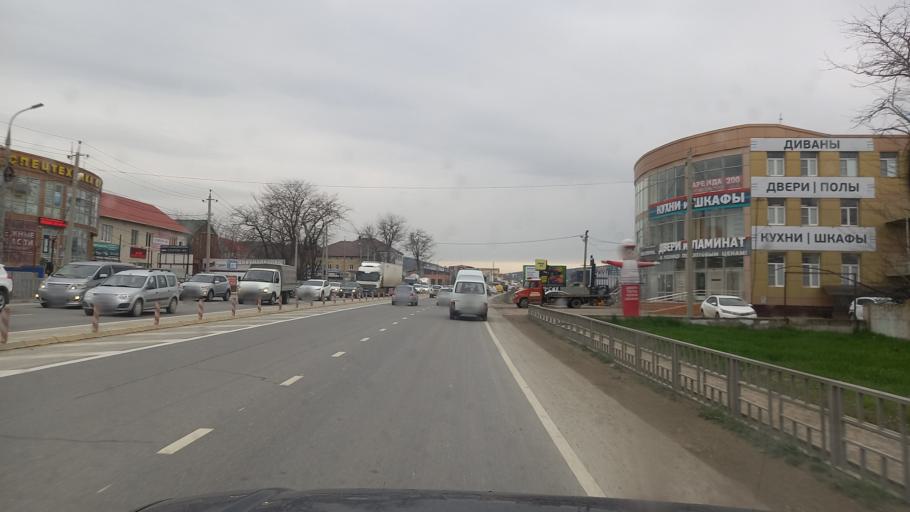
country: RU
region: Krasnodarskiy
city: Gayduk
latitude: 44.7692
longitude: 37.6998
